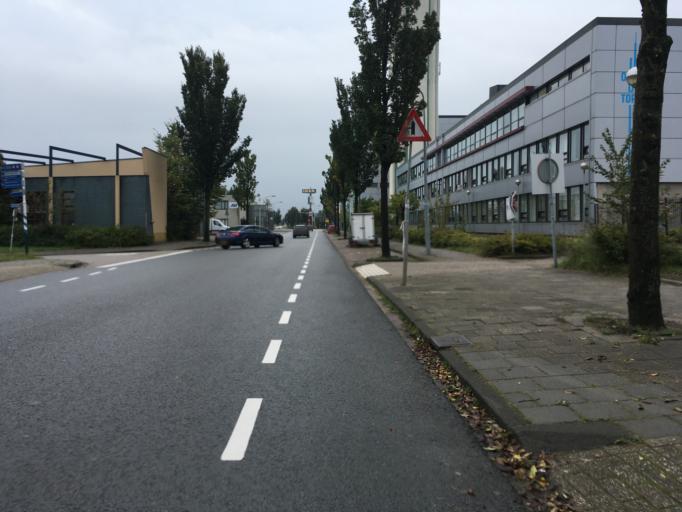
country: NL
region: North Holland
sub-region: Gemeente Haarlem
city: Haarlem
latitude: 52.3894
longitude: 4.6692
